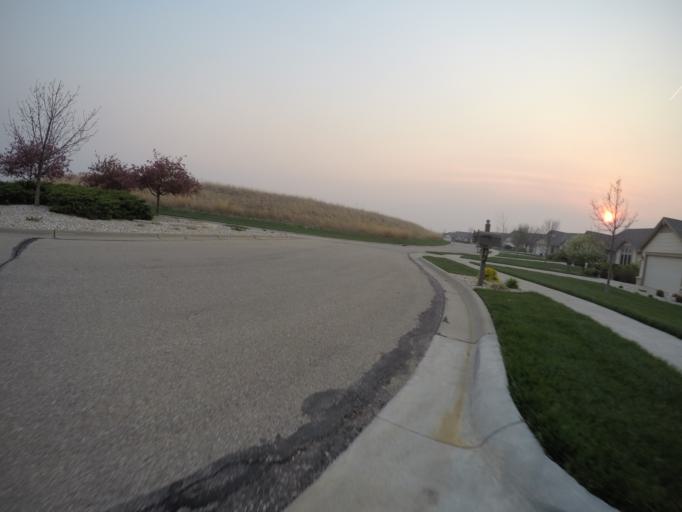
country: US
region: Kansas
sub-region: Riley County
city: Manhattan
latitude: 39.2044
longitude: -96.6378
